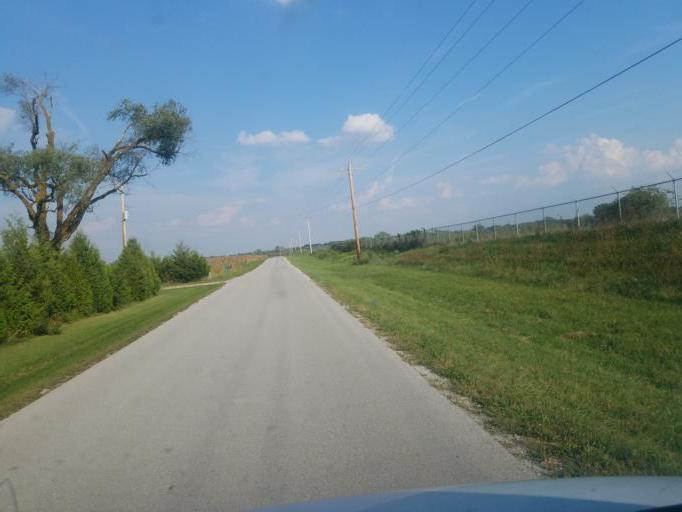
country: US
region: Ohio
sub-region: Wyandot County
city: Carey
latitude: 40.9200
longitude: -83.3344
